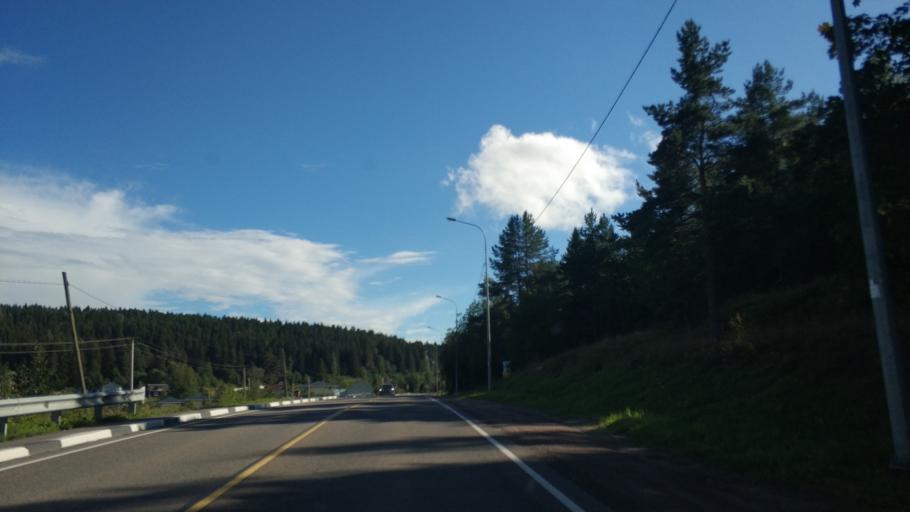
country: RU
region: Republic of Karelia
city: Sortavala
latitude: 61.6619
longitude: 30.6556
